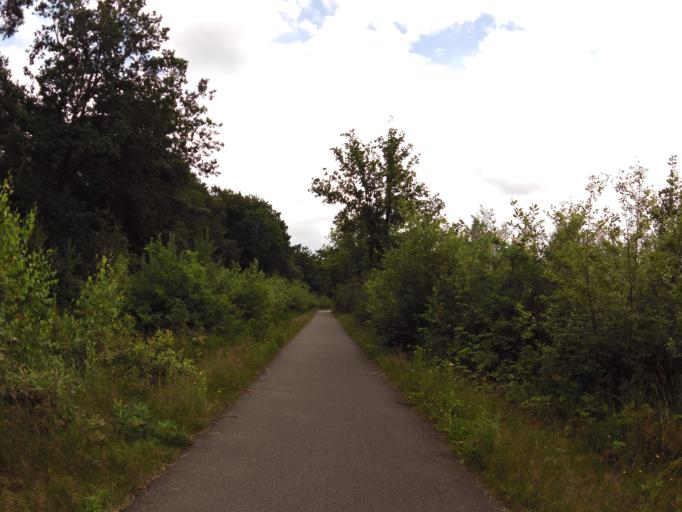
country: NL
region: North Brabant
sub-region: Gemeente Valkenswaard
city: Valkenswaard
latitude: 51.3257
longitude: 5.4511
